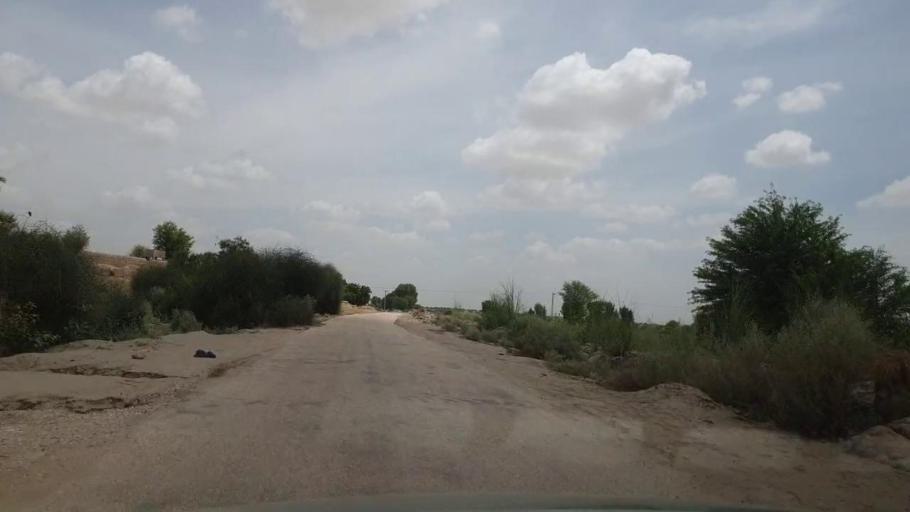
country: PK
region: Sindh
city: Kot Diji
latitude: 27.2091
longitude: 69.1160
